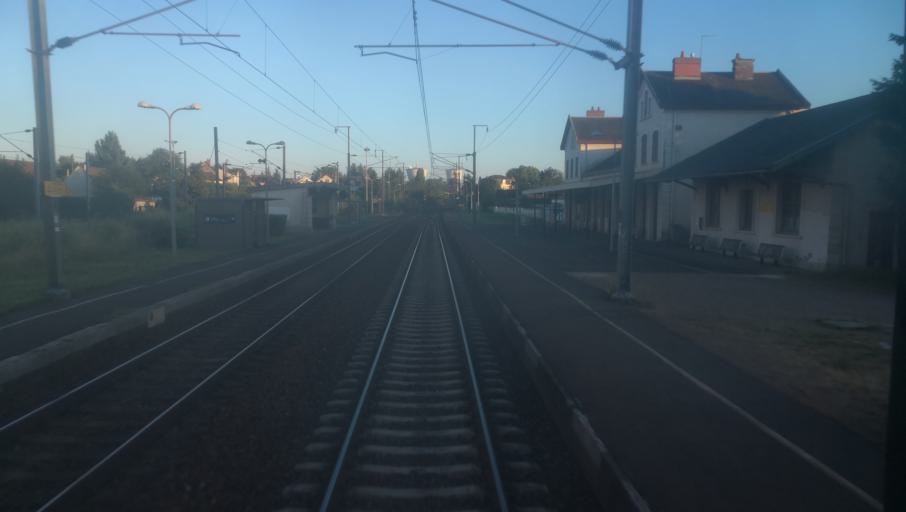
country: FR
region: Bourgogne
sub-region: Departement de la Nievre
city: La Charite-sur-Loire
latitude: 47.1805
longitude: 3.0243
